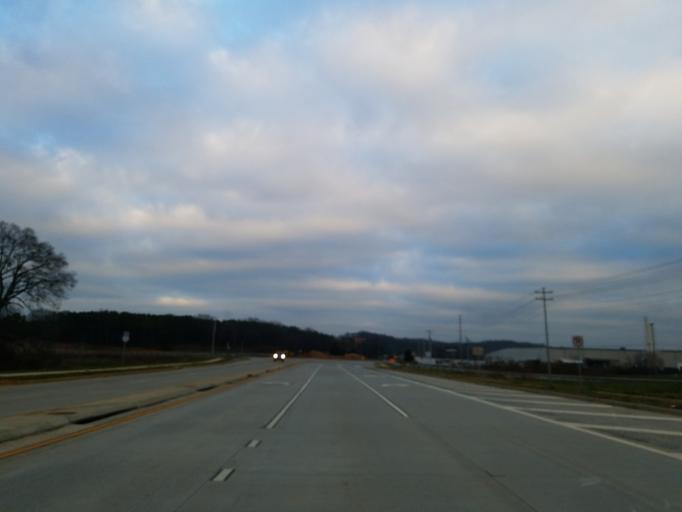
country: US
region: Georgia
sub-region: Gordon County
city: Calhoun
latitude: 34.4420
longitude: -84.9162
